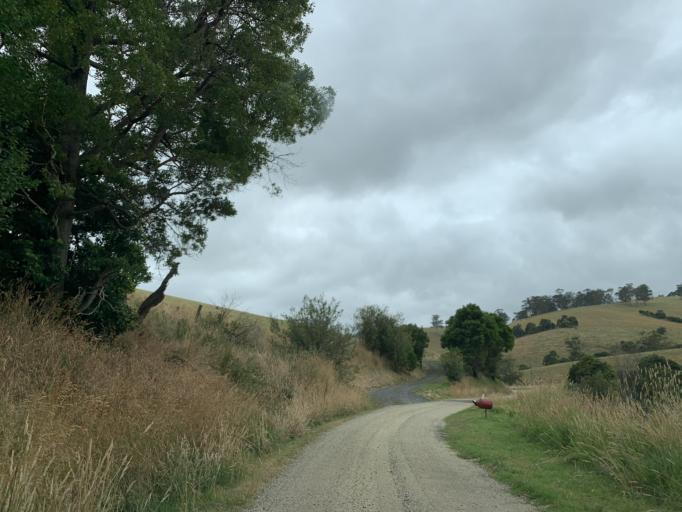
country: AU
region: Victoria
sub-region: Baw Baw
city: Warragul
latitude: -38.2889
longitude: 145.8701
